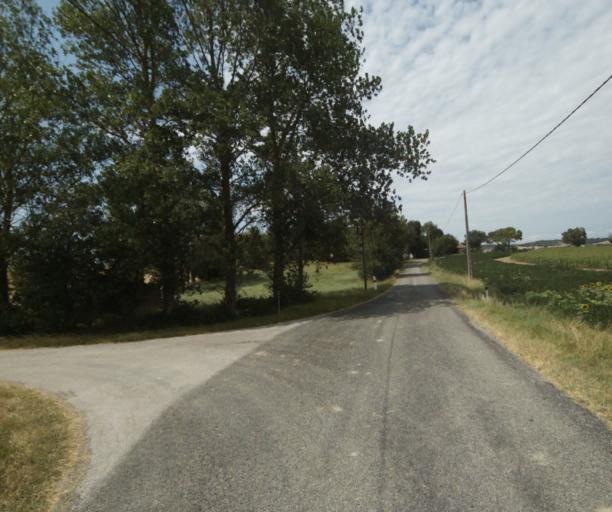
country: FR
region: Midi-Pyrenees
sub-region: Departement de la Haute-Garonne
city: Saint-Felix-Lauragais
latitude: 43.4222
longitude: 1.9101
